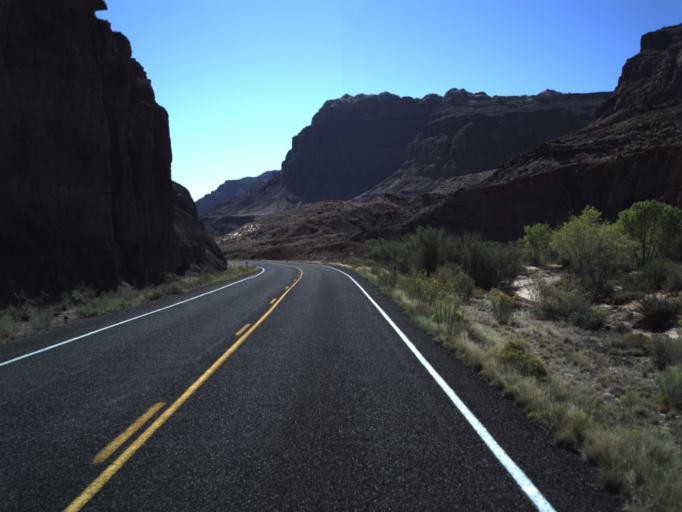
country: US
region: Utah
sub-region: San Juan County
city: Blanding
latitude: 37.9083
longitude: -110.4571
